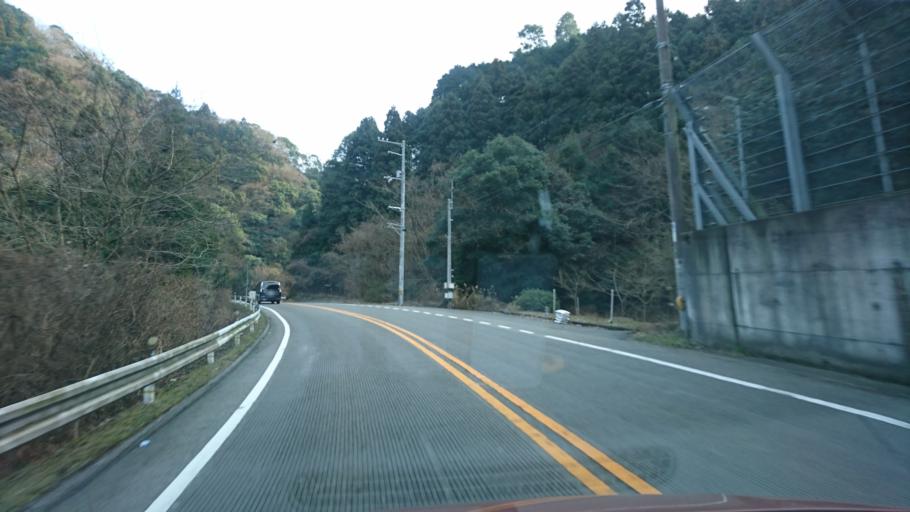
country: JP
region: Ehime
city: Hojo
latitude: 33.9592
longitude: 132.9094
